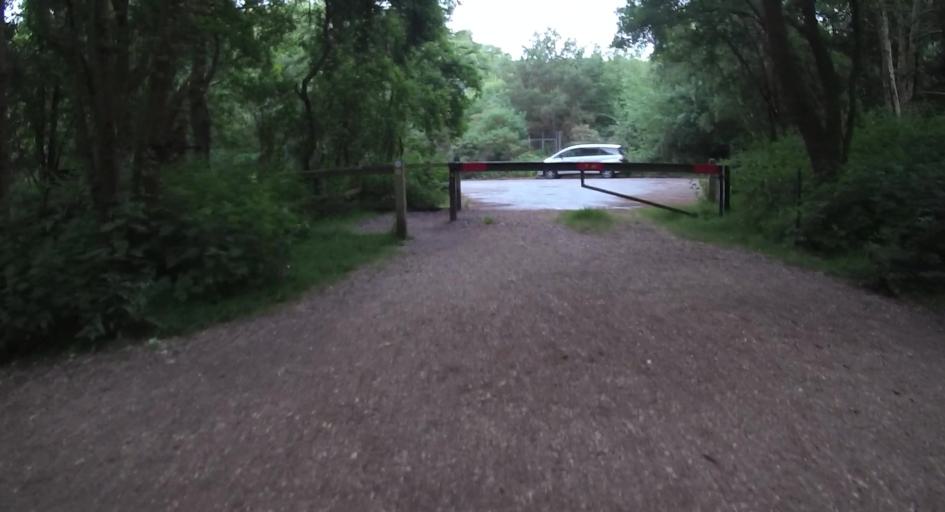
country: GB
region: England
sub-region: Hampshire
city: Farnborough
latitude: 51.2838
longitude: -0.7925
